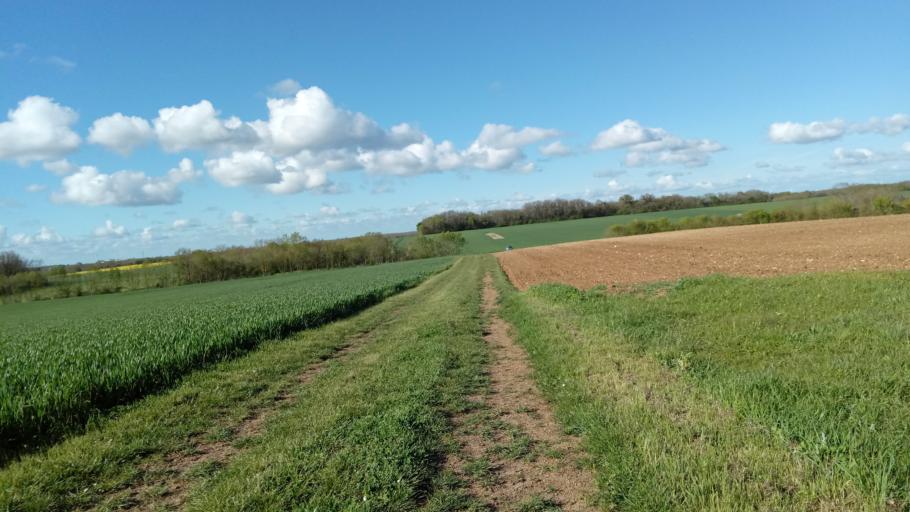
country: FR
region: Poitou-Charentes
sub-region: Departement de la Charente-Maritime
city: Verines
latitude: 46.1591
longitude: -0.9376
